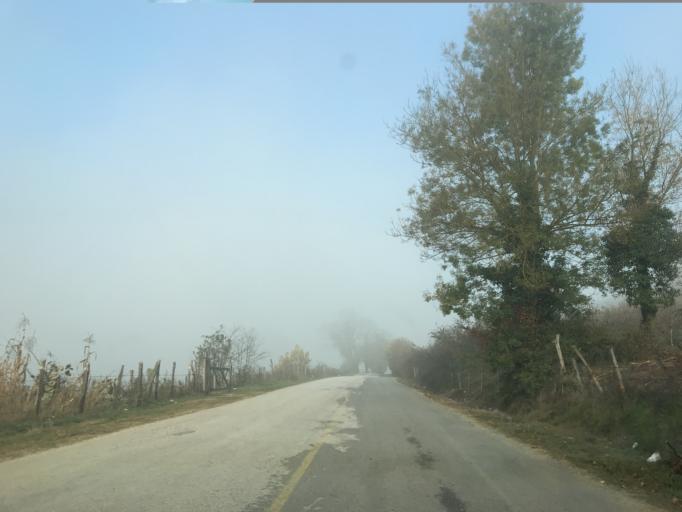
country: TR
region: Duzce
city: Cumayeri
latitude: 40.8968
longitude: 30.9530
